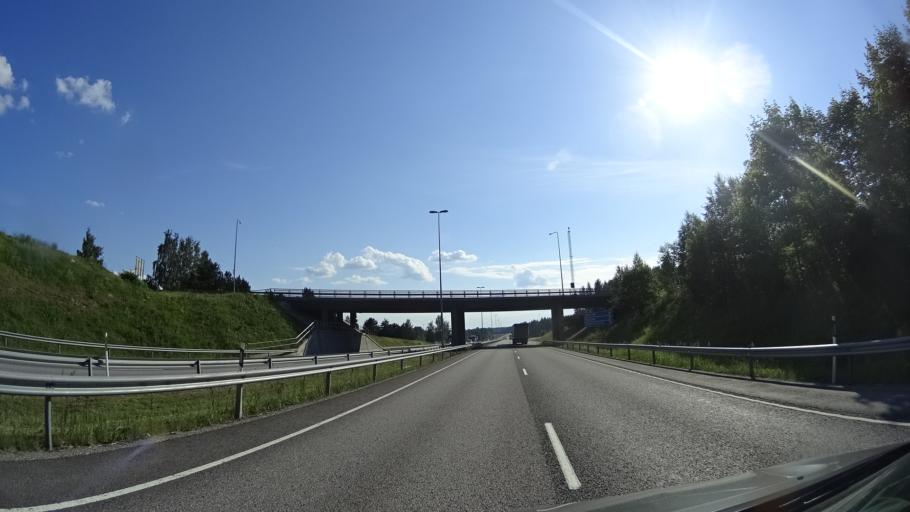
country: FI
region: South Karelia
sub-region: Imatra
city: Imatra
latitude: 61.1733
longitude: 28.7017
